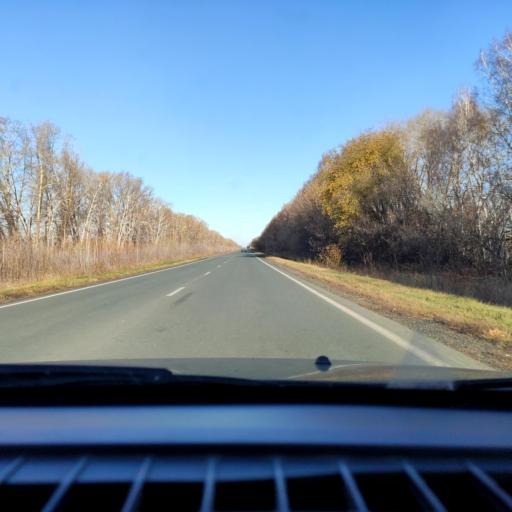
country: RU
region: Samara
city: Tol'yatti
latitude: 53.6013
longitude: 49.3222
